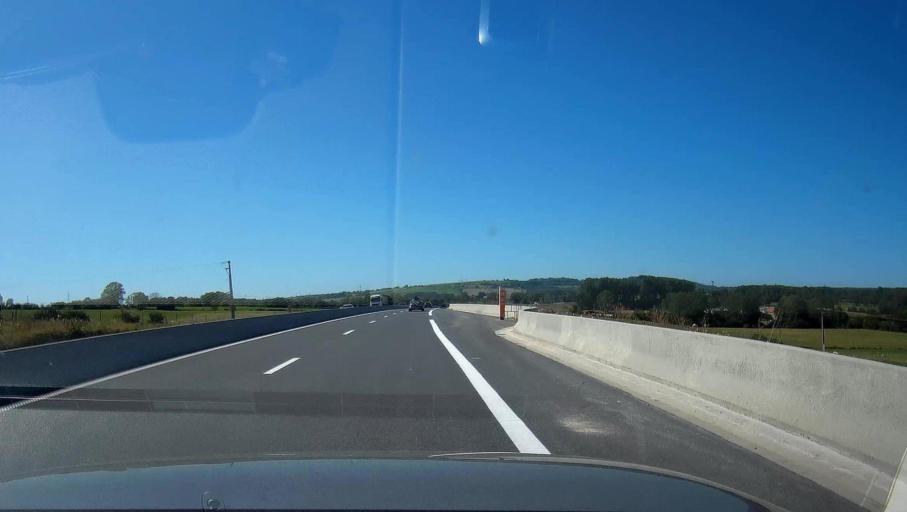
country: FR
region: Champagne-Ardenne
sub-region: Departement des Ardennes
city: Rimogne
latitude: 49.7909
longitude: 4.5498
